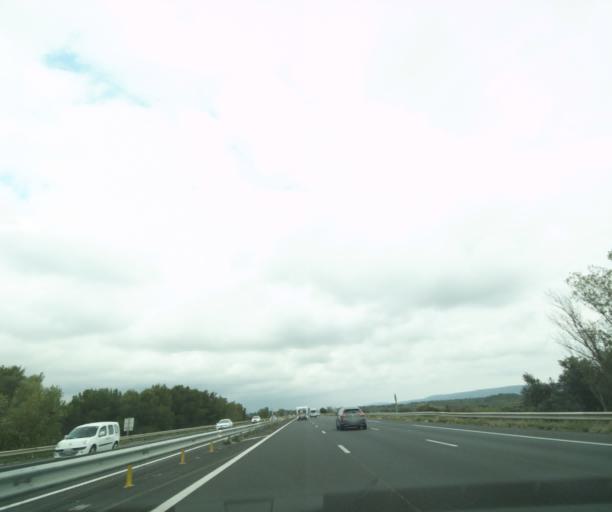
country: FR
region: Languedoc-Roussillon
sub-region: Departement de l'Herault
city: Bouzigues
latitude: 43.4675
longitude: 3.6371
